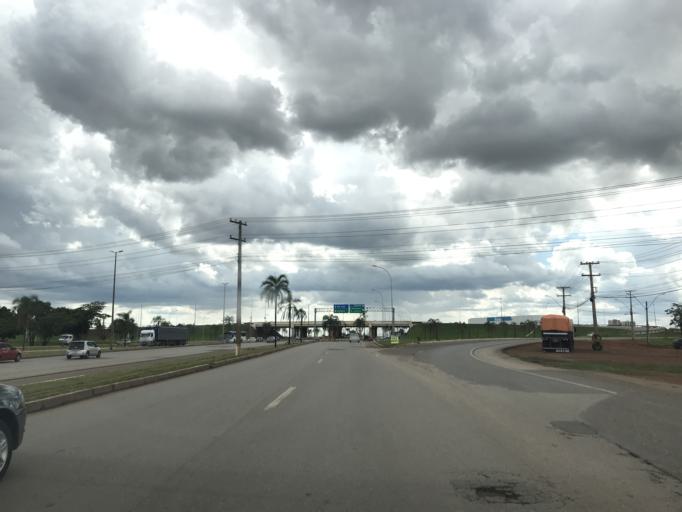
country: BR
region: Federal District
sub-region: Brasilia
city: Brasilia
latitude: -15.8812
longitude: -48.0578
